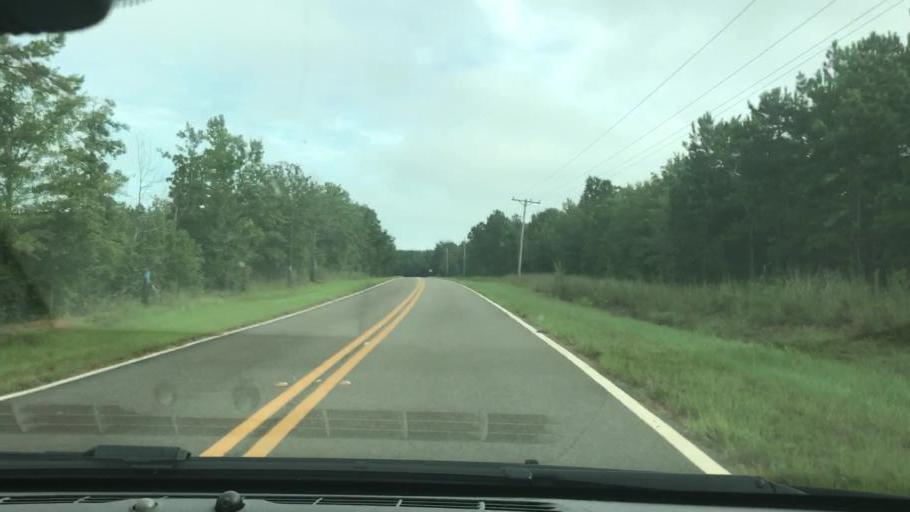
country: US
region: Georgia
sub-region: Stewart County
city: Lumpkin
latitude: 32.0386
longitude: -84.9096
